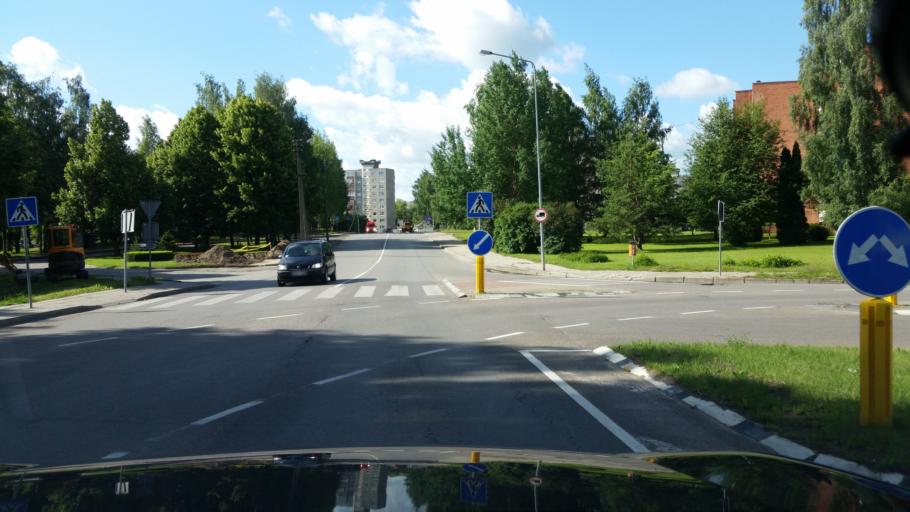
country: LT
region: Marijampoles apskritis
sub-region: Marijampole Municipality
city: Marijampole
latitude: 54.5674
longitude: 23.3401
